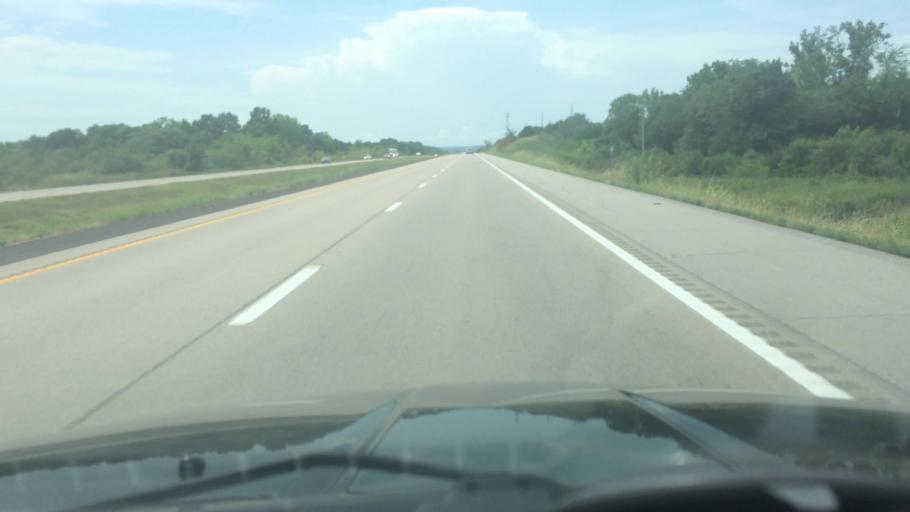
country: US
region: Missouri
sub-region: Polk County
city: Humansville
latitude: 37.7719
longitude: -93.5667
